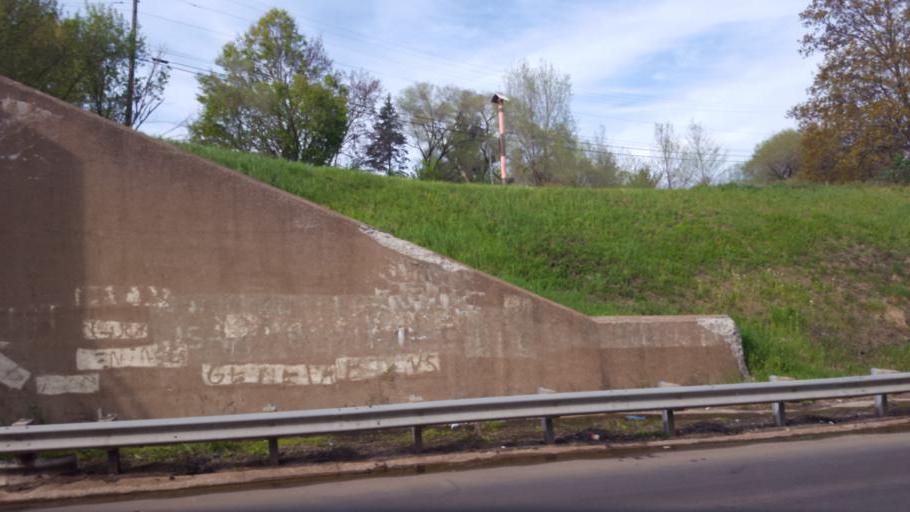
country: US
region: Ohio
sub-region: Ashtabula County
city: Geneva
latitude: 41.7994
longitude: -80.9671
